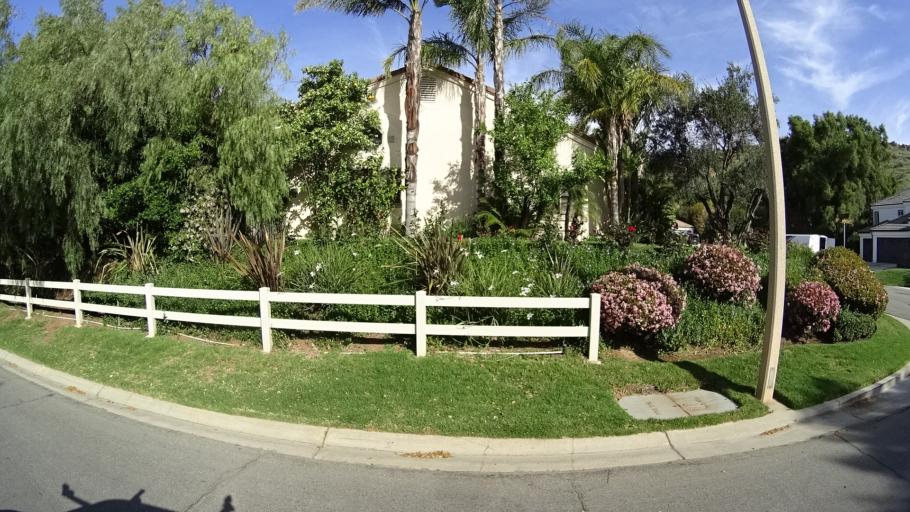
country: US
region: California
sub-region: Ventura County
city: Oak Park
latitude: 34.1939
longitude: -118.7912
